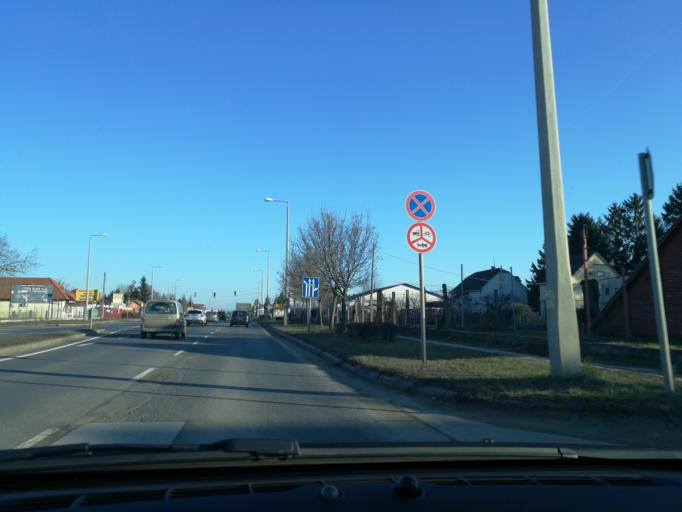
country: HU
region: Szabolcs-Szatmar-Bereg
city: Nyiregyhaza
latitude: 47.9512
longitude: 21.7584
